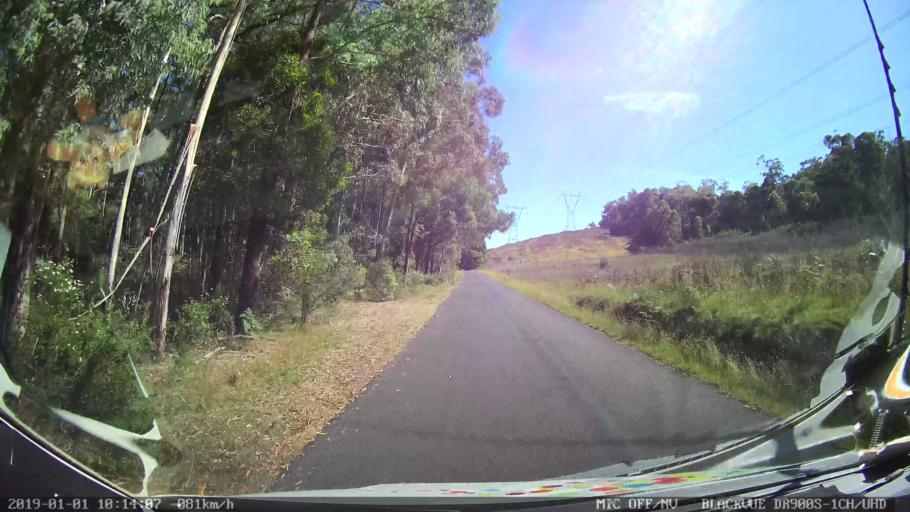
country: AU
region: New South Wales
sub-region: Snowy River
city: Jindabyne
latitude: -36.1158
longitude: 148.1609
